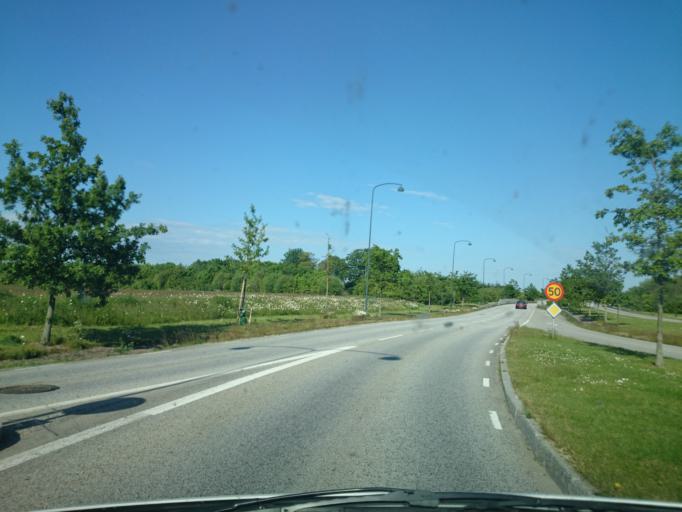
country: SE
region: Skane
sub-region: Lunds Kommun
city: Lund
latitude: 55.7191
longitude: 13.2354
